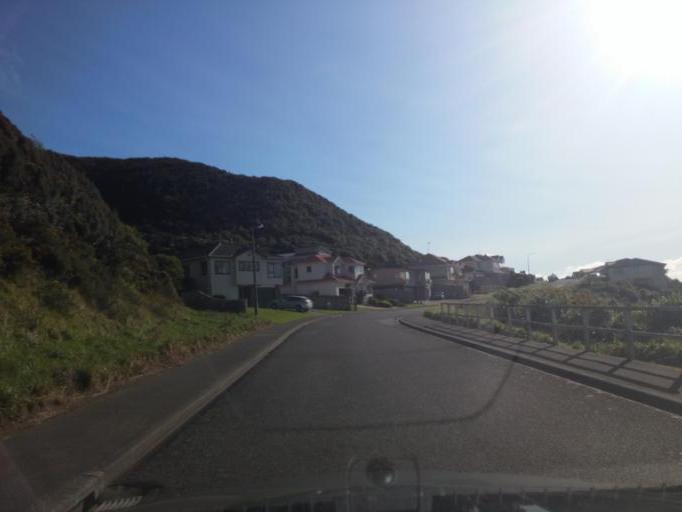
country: NZ
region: Wellington
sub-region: Wellington City
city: Wellington
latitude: -41.2352
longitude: 174.7918
